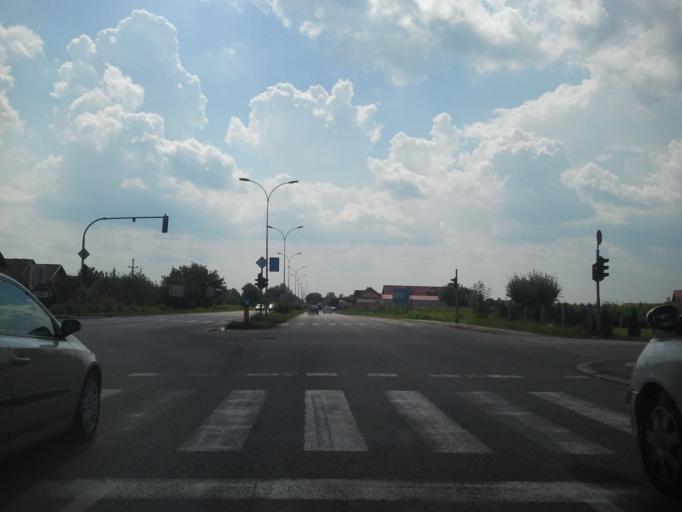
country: RS
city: Veternik
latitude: 45.2464
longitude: 19.7366
